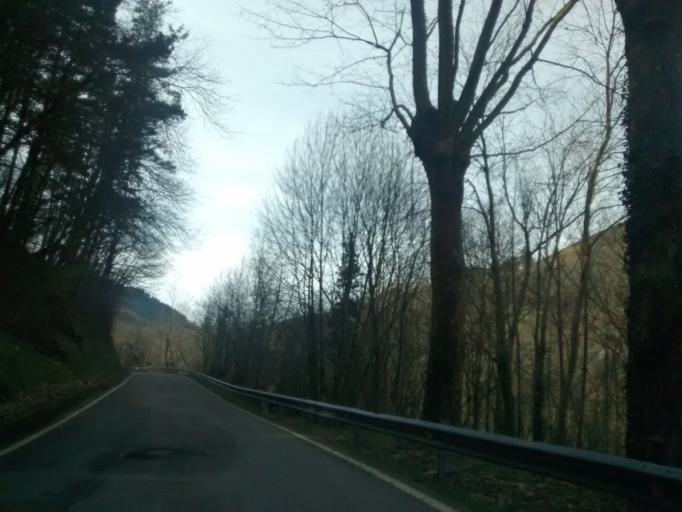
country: ES
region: Cantabria
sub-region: Provincia de Cantabria
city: Vega de Pas
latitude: 43.1587
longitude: -3.8126
